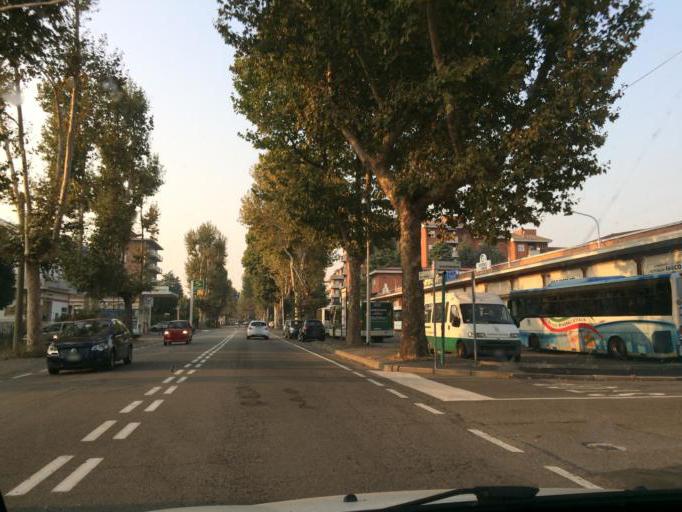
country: IT
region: Lombardy
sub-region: Provincia di Varese
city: Castellanza
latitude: 45.6083
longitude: 8.8899
